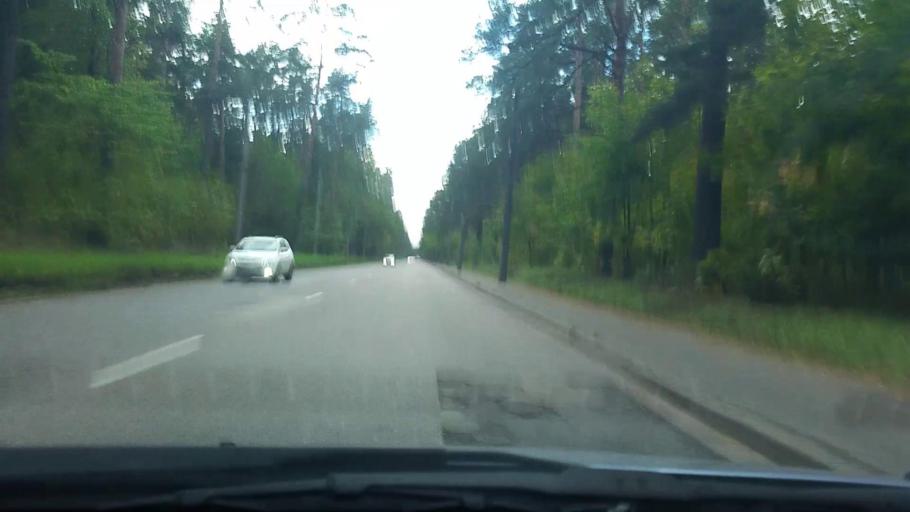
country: LV
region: Stopini
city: Ulbroka
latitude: 56.9617
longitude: 24.2222
